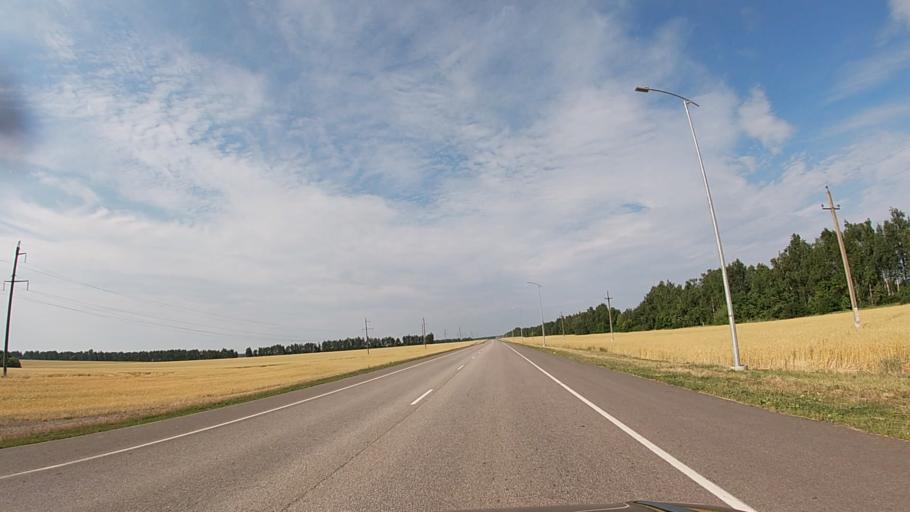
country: RU
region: Belgorod
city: Proletarskiy
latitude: 50.8267
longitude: 35.7611
